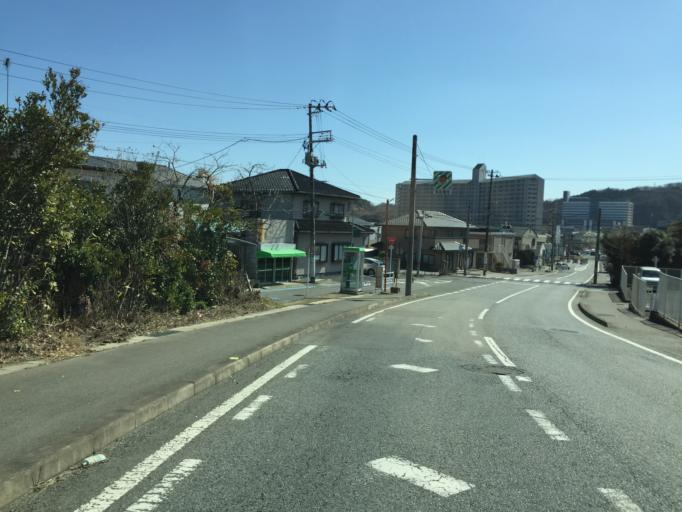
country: JP
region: Fukushima
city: Iwaki
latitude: 37.0476
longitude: 140.8609
